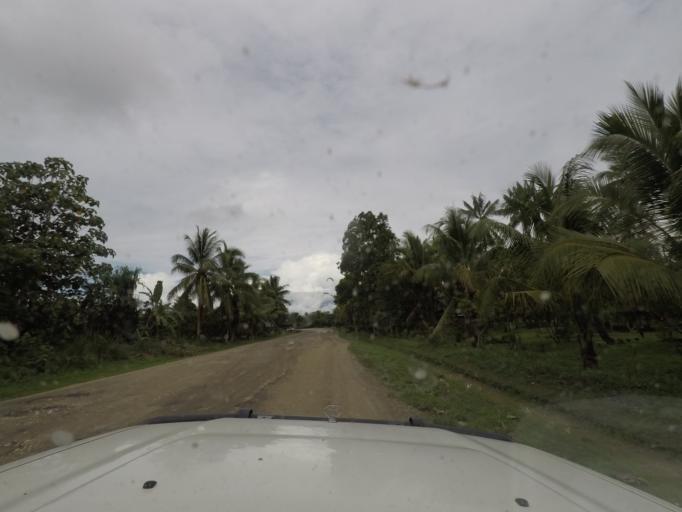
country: PG
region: Eastern Highlands
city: Goroka
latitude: -5.6369
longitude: 145.4862
